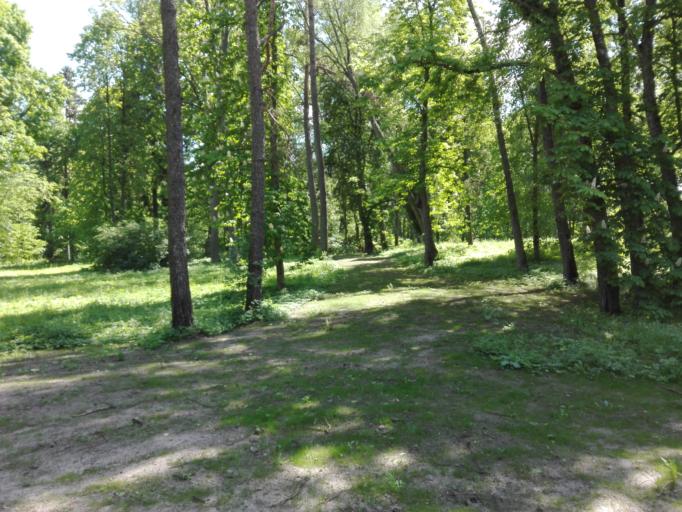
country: LT
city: Trakai
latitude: 54.6625
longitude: 24.9447
